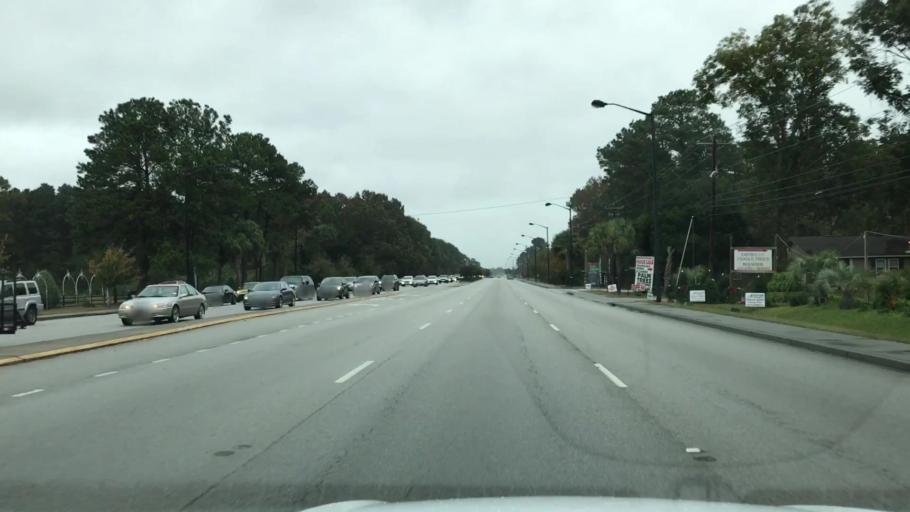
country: US
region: South Carolina
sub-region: Charleston County
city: Isle of Palms
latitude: 32.8482
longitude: -79.8094
